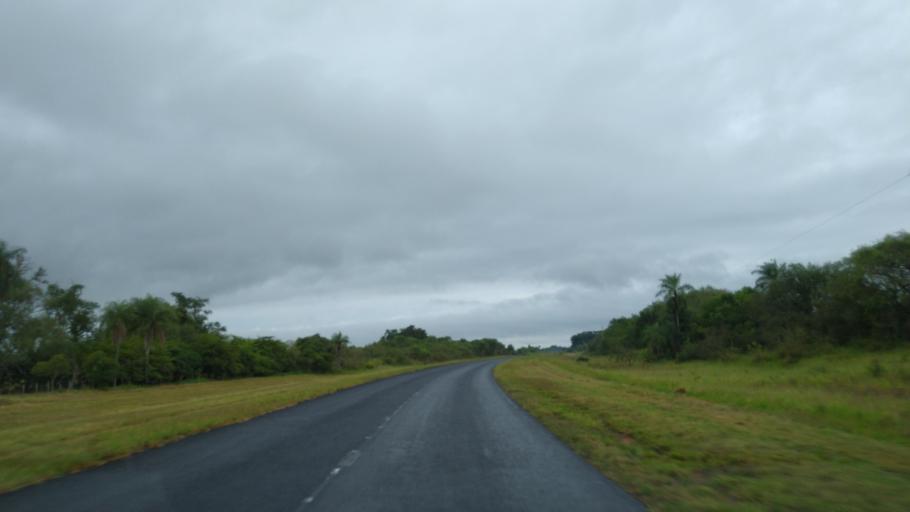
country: AR
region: Corrientes
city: Loreto
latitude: -27.7073
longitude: -57.2277
